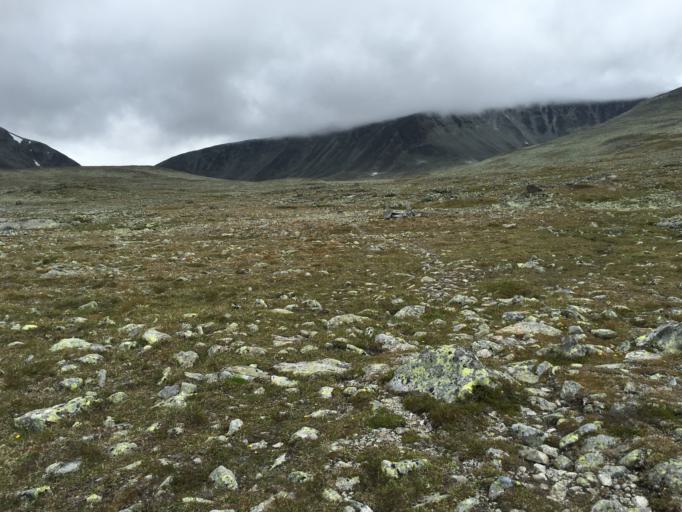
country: NO
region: Oppland
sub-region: Lom
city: Fossbergom
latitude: 61.5841
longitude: 8.7198
